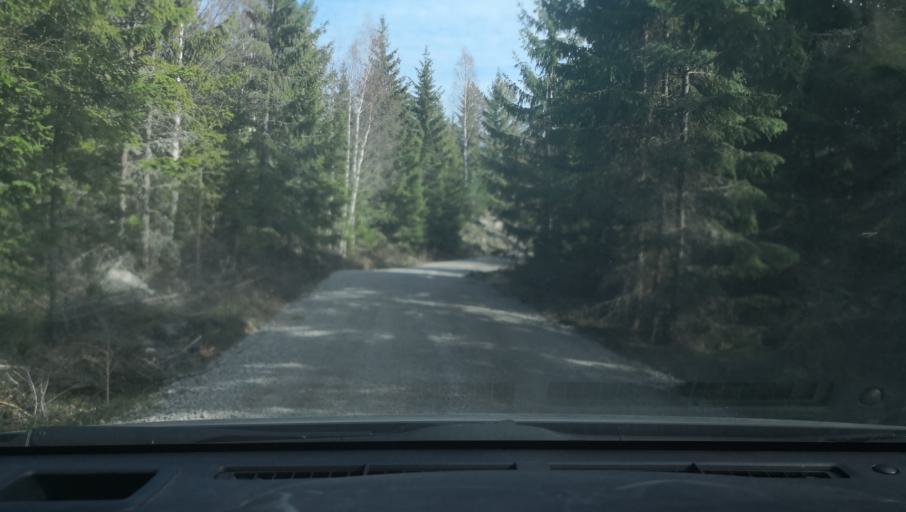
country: SE
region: Uppsala
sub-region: Heby Kommun
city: Heby
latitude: 59.8410
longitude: 16.8589
